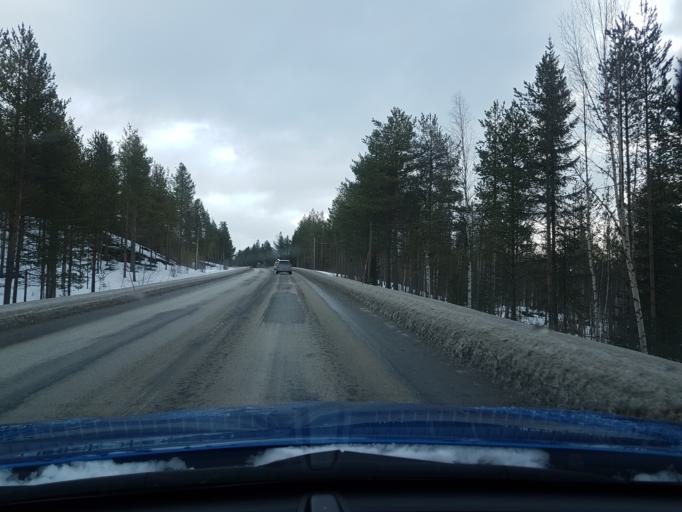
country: SE
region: Jaemtland
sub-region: Harjedalens Kommun
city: Sveg
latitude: 62.4167
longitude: 13.5501
